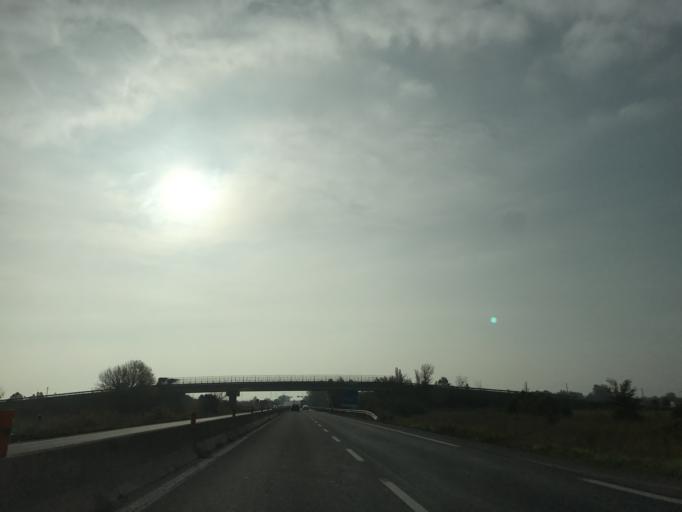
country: IT
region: Emilia-Romagna
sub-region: Forli-Cesena
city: Gatteo a Mare
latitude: 44.1746
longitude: 12.4171
